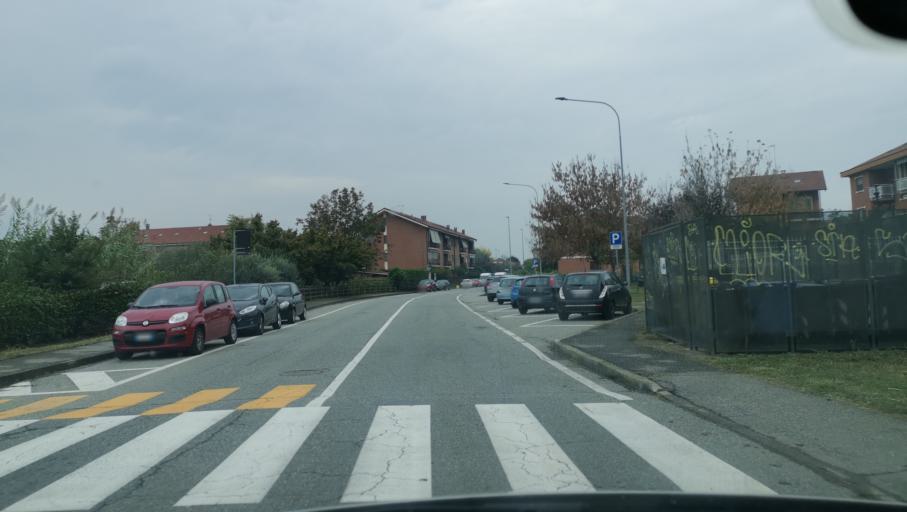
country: IT
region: Piedmont
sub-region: Provincia di Torino
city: Settimo Torinese
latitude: 45.1297
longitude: 7.7687
